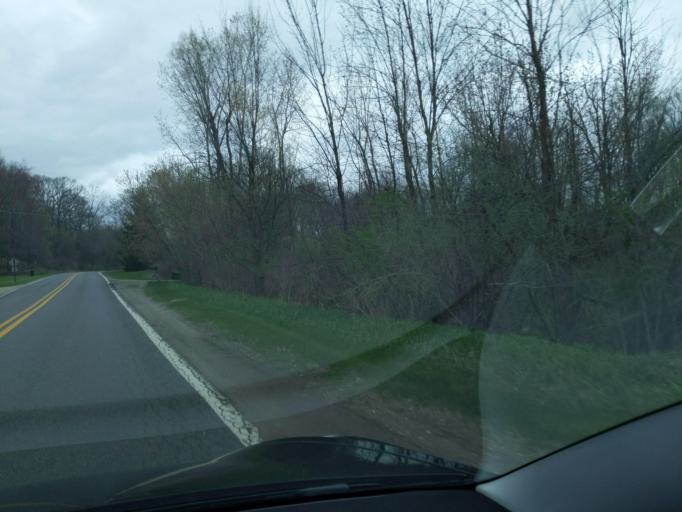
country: US
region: Michigan
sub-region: Ingham County
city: Stockbridge
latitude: 42.4426
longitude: -84.0980
